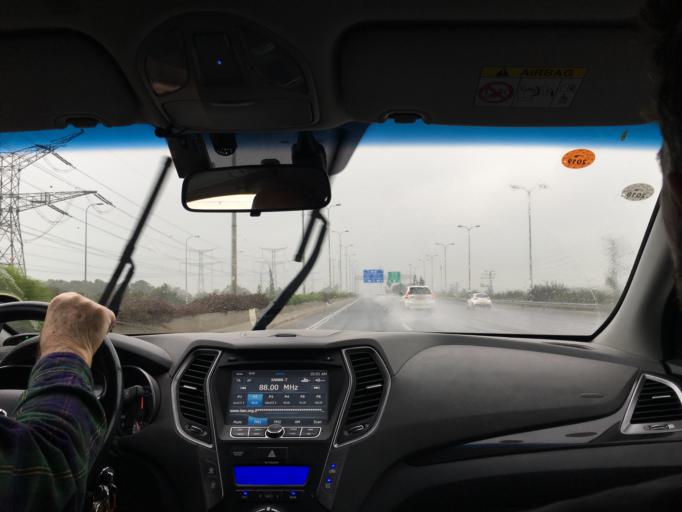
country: IL
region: Central District
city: Petah Tiqwa
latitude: 32.1223
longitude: 34.8965
